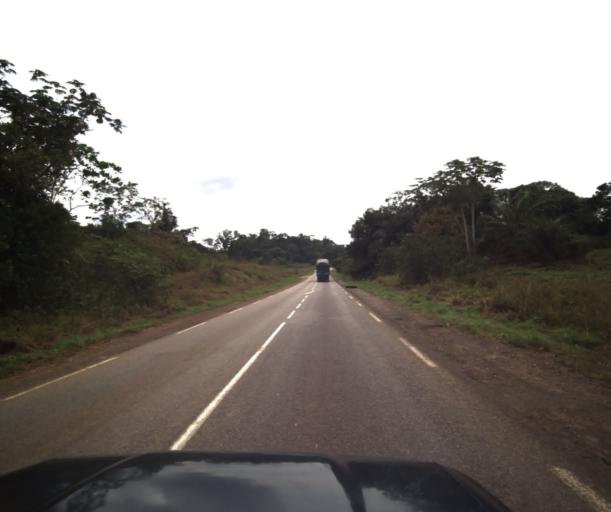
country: CM
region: Littoral
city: Edea
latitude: 3.8310
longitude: 10.4007
